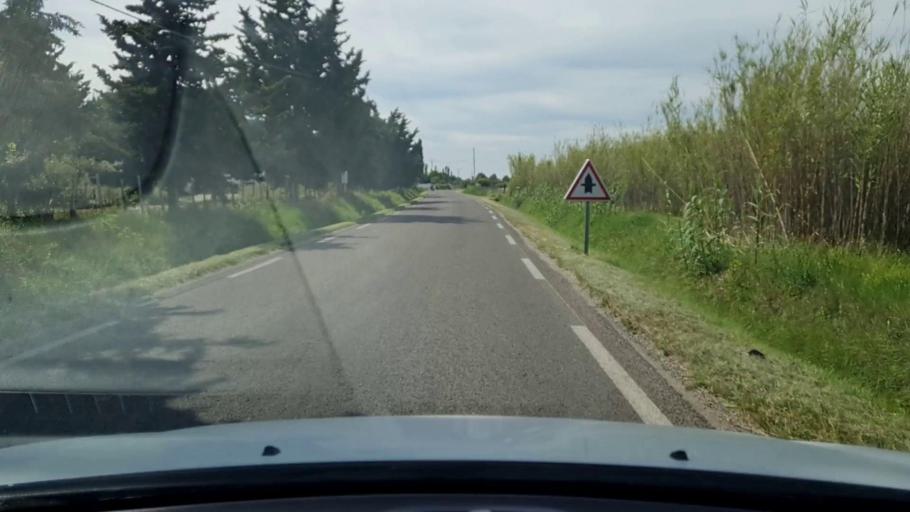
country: FR
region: Languedoc-Roussillon
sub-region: Departement du Gard
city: Aigues-Mortes
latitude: 43.6166
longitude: 4.2059
